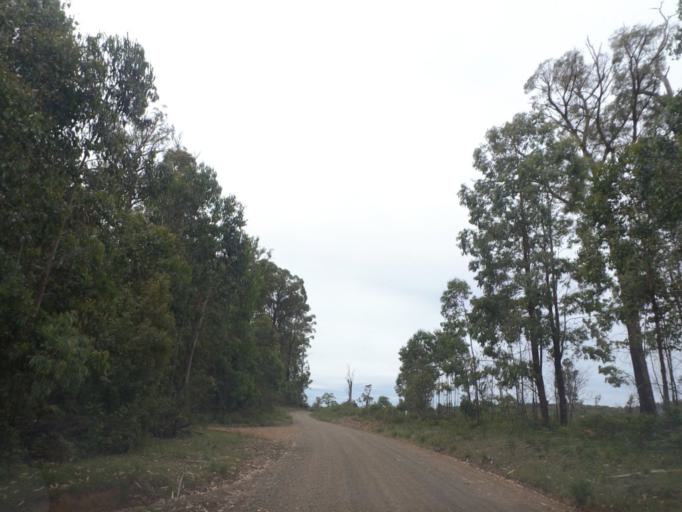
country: AU
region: Victoria
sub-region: Murrindindi
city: Alexandra
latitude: -37.4056
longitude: 145.5918
